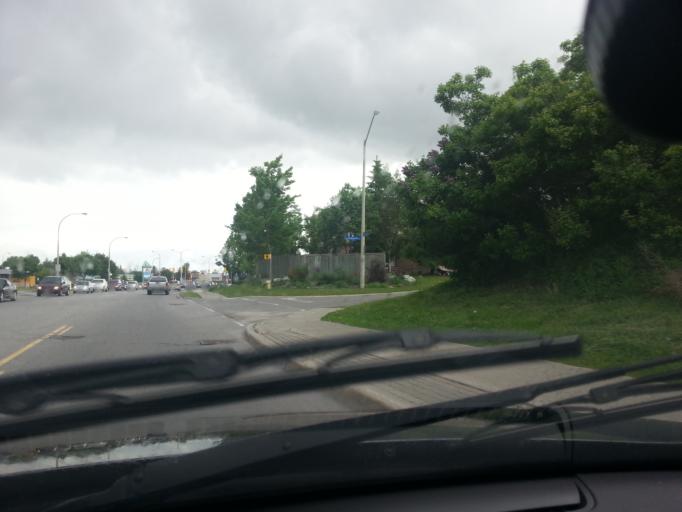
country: CA
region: Ontario
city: Bells Corners
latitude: 45.2660
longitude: -75.9293
